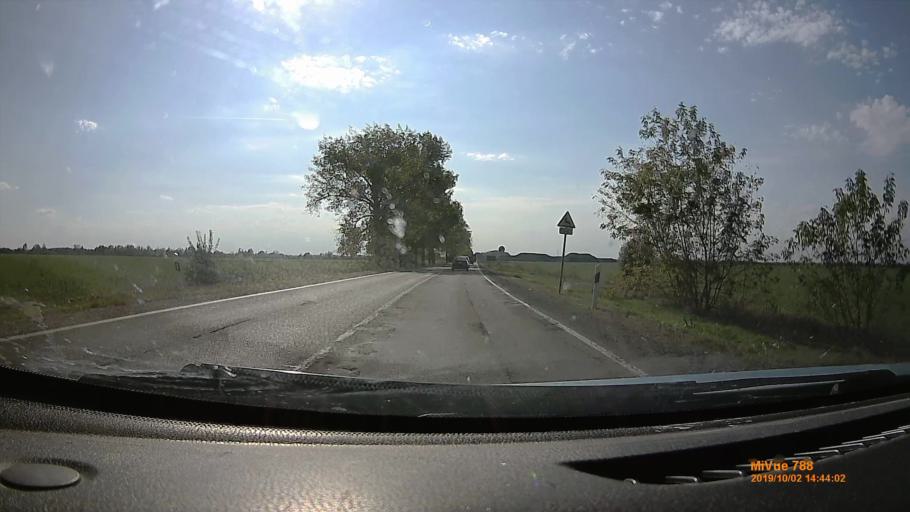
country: HU
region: Heves
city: Szihalom
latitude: 47.7696
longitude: 20.4589
